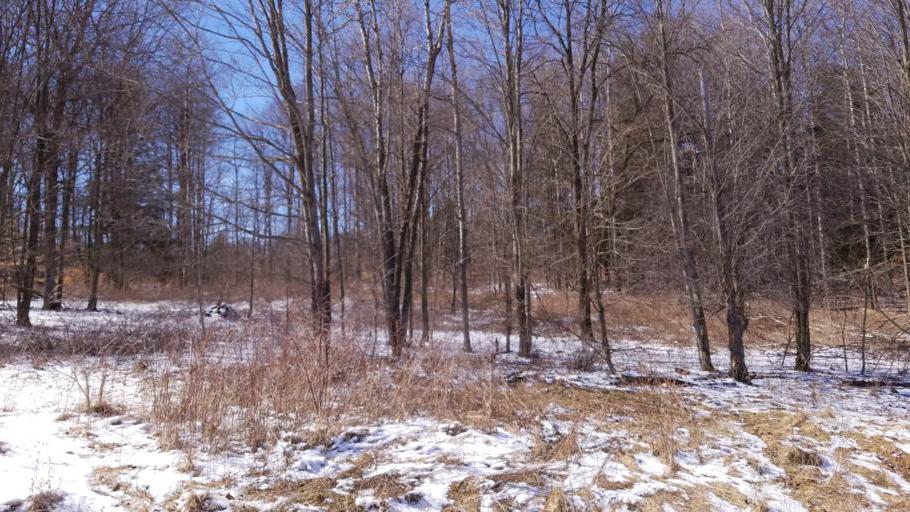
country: US
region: Pennsylvania
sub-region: Tioga County
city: Westfield
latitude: 41.9574
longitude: -77.7273
